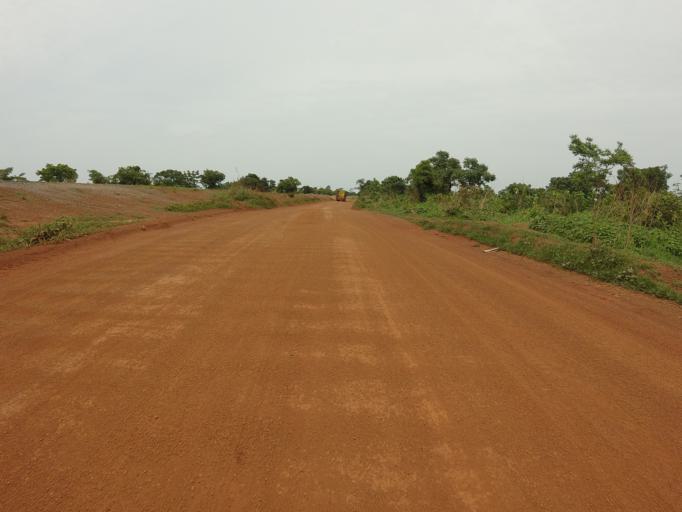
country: GH
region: Northern
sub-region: Yendi
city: Yendi
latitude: 8.9813
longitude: -0.0162
